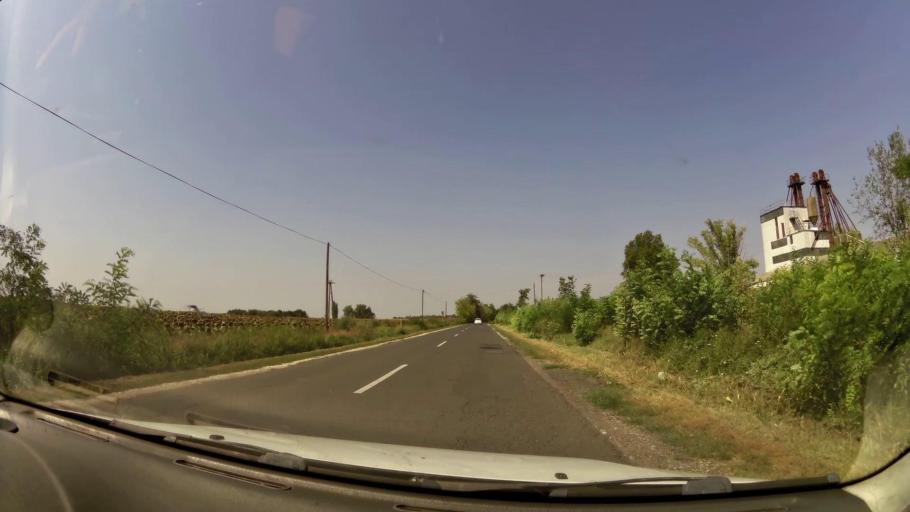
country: HU
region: Pest
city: Tapioszentmarton
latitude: 47.3473
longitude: 19.7187
